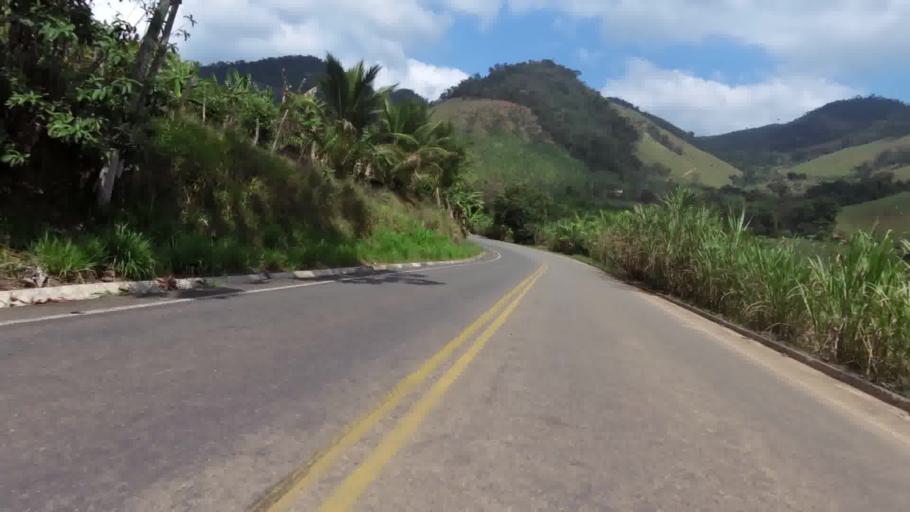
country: BR
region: Espirito Santo
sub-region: Alfredo Chaves
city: Alfredo Chaves
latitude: -20.6171
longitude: -40.7788
